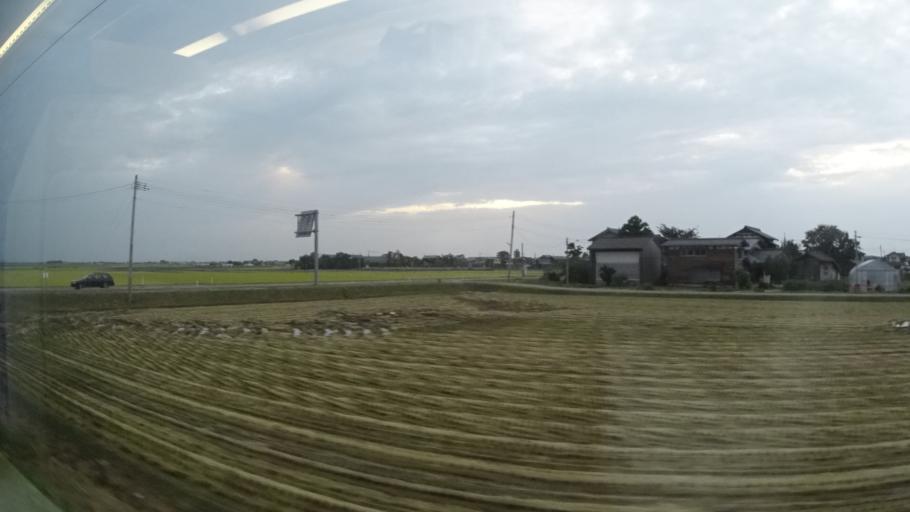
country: JP
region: Niigata
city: Murakami
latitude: 38.1729
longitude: 139.4594
